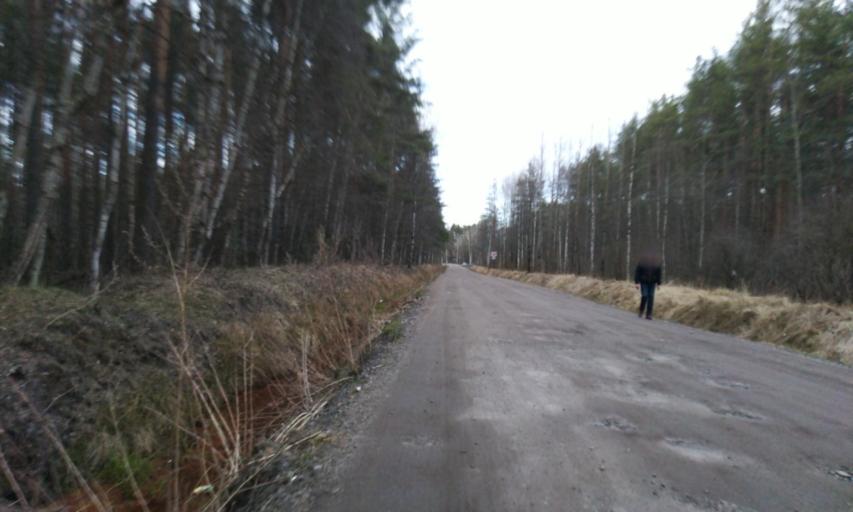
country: RU
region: Leningrad
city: Toksovo
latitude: 60.1163
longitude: 30.4808
